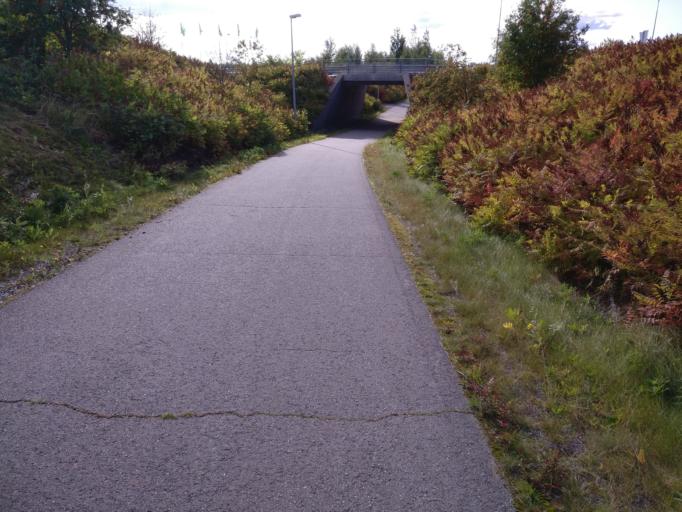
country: FI
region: Pirkanmaa
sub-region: Tampere
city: Lempaeaelae
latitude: 61.3662
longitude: 23.7991
